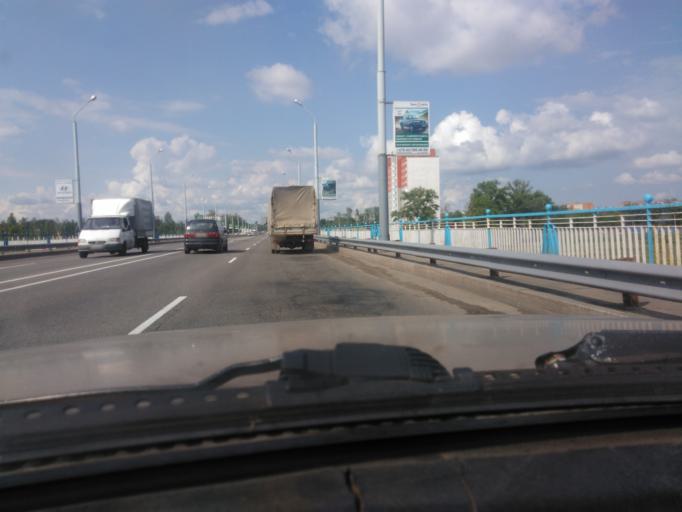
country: BY
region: Mogilev
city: Mahilyow
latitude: 53.9208
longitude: 30.3494
